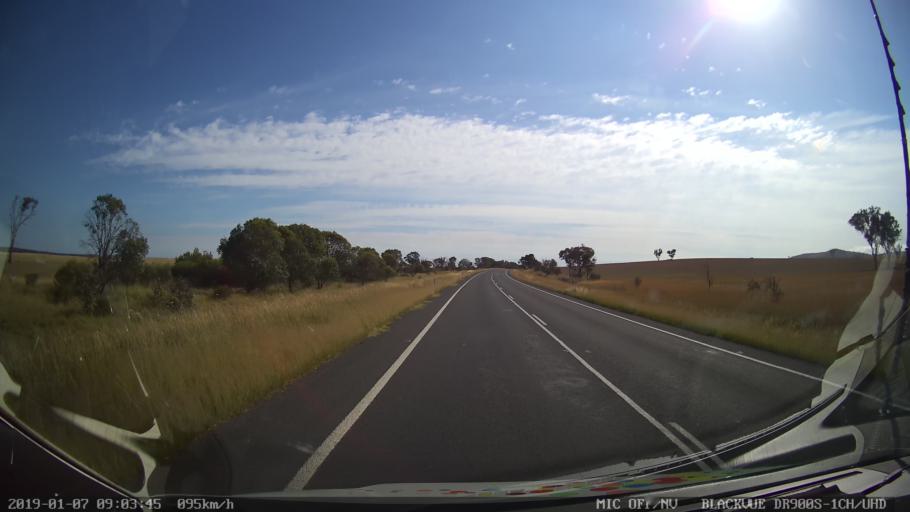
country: AU
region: New South Wales
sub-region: Armidale Dumaresq
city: Armidale
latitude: -30.7260
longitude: 151.4417
